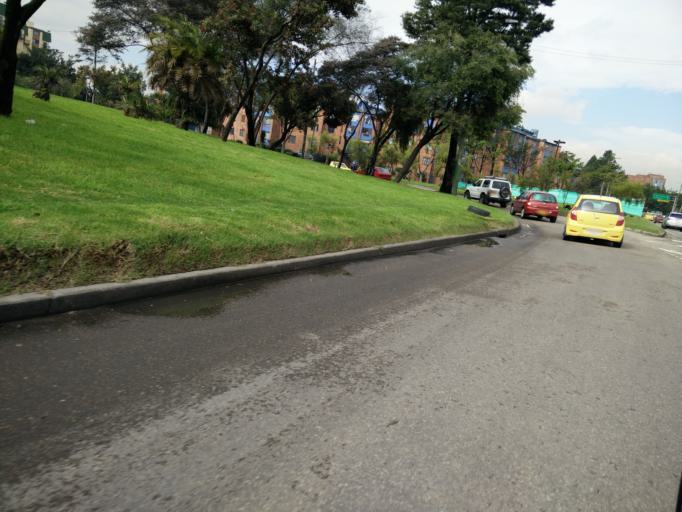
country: CO
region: Bogota D.C.
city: Bogota
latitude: 4.6609
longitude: -74.1122
